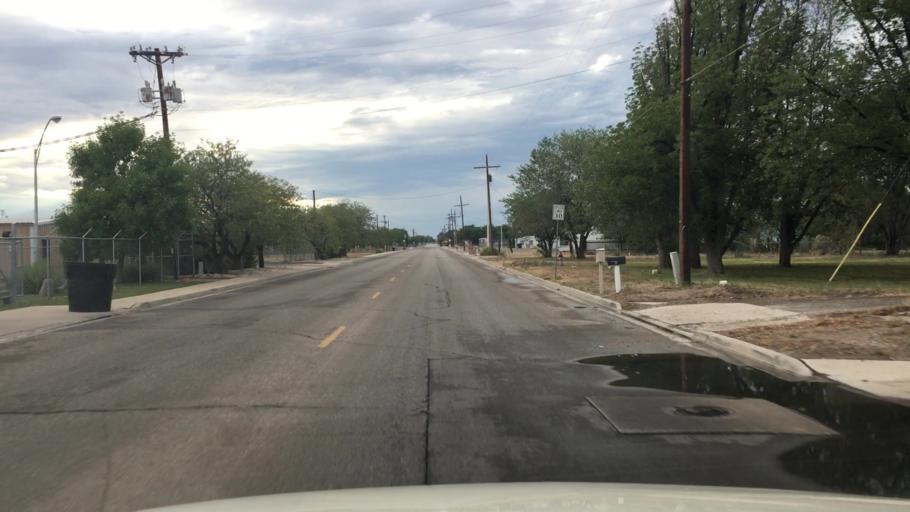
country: US
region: New Mexico
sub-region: Chaves County
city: Roswell
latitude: 33.4160
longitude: -104.5071
